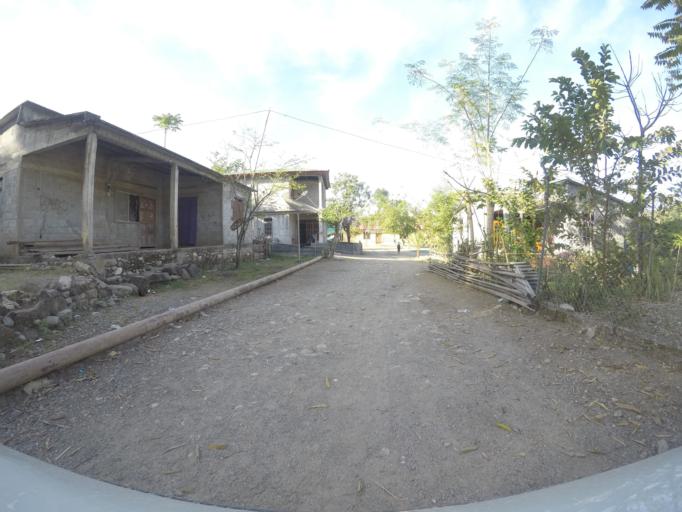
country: TL
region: Viqueque
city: Viqueque
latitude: -8.8311
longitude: 126.3732
